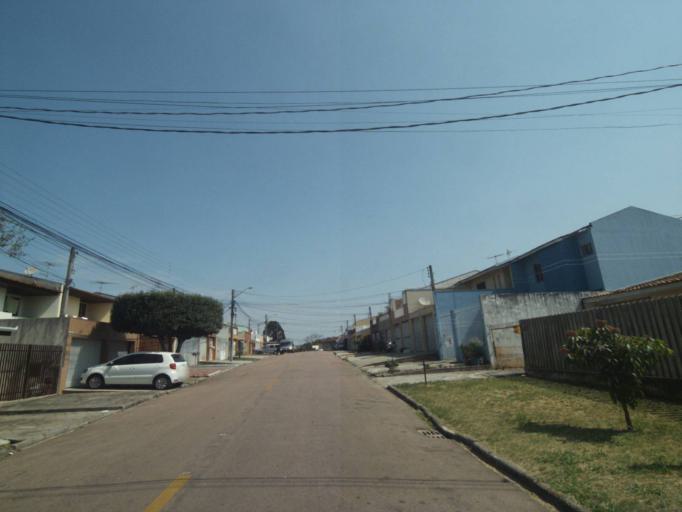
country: BR
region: Parana
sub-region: Curitiba
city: Curitiba
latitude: -25.4817
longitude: -49.3215
